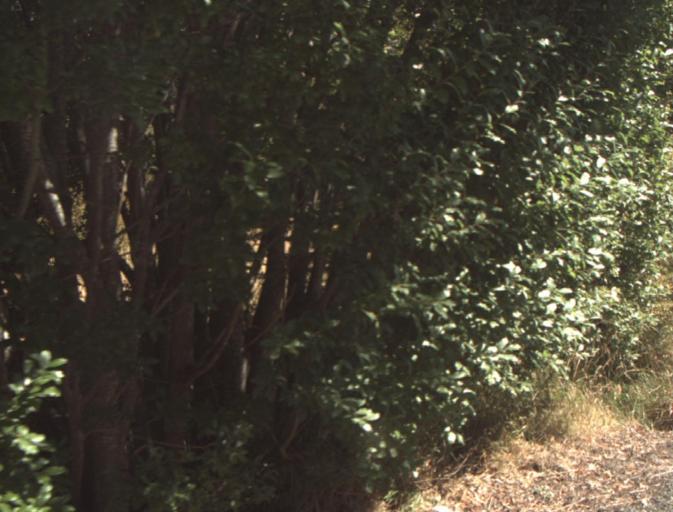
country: AU
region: Tasmania
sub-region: Launceston
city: Newstead
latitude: -41.3568
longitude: 147.3028
